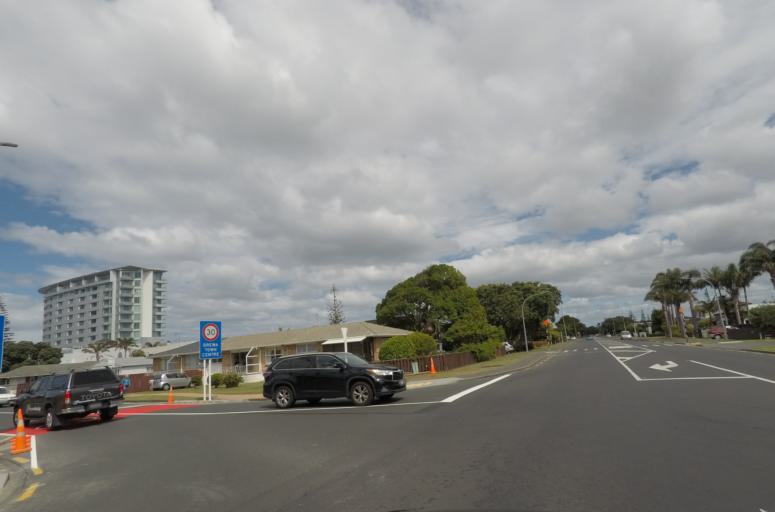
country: NZ
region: Auckland
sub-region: Auckland
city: Rothesay Bay
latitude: -36.5872
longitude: 174.6922
